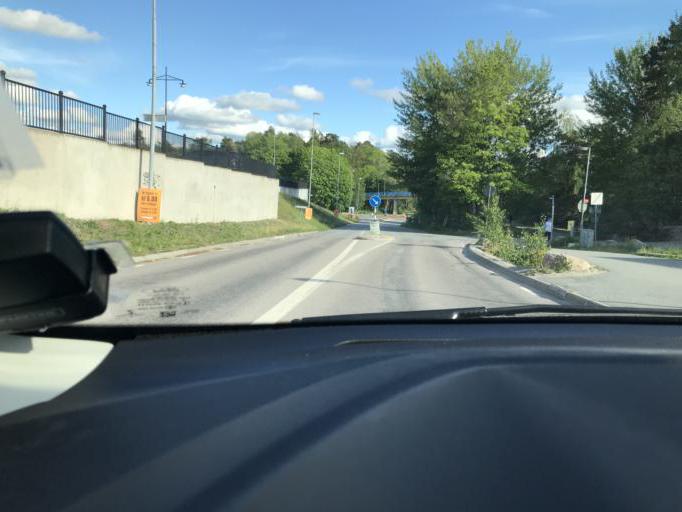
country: SE
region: Stockholm
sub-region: Botkyrka Kommun
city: Fittja
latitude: 59.2521
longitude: 17.8638
